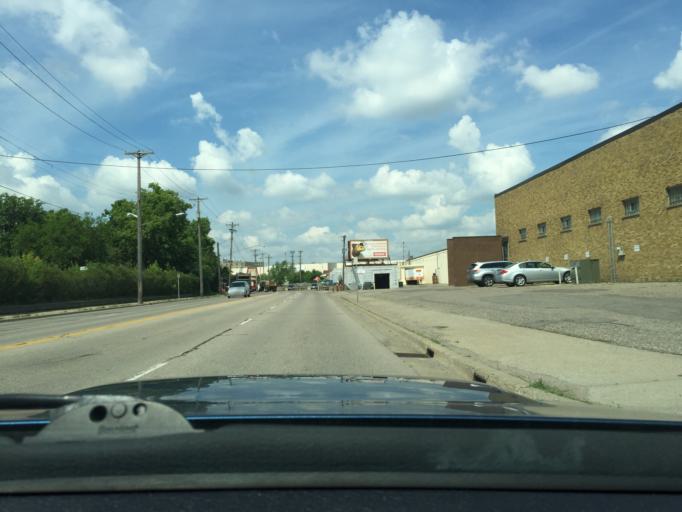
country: US
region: Minnesota
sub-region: Hennepin County
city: Minneapolis
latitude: 44.9916
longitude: -93.2447
